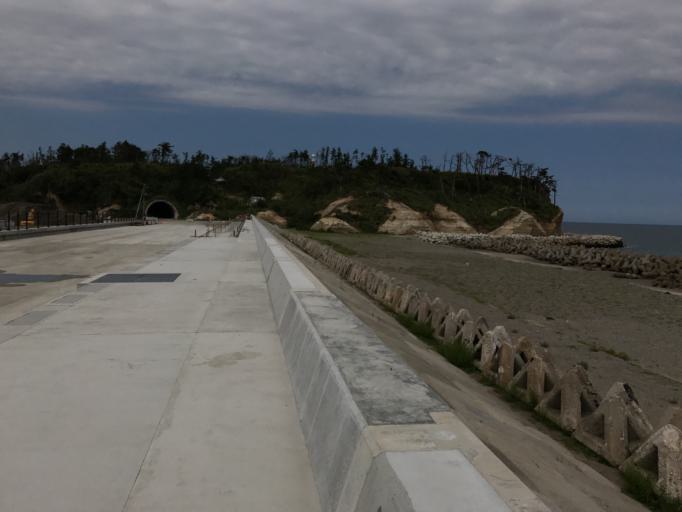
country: JP
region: Miyagi
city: Marumori
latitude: 37.8206
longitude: 140.9857
